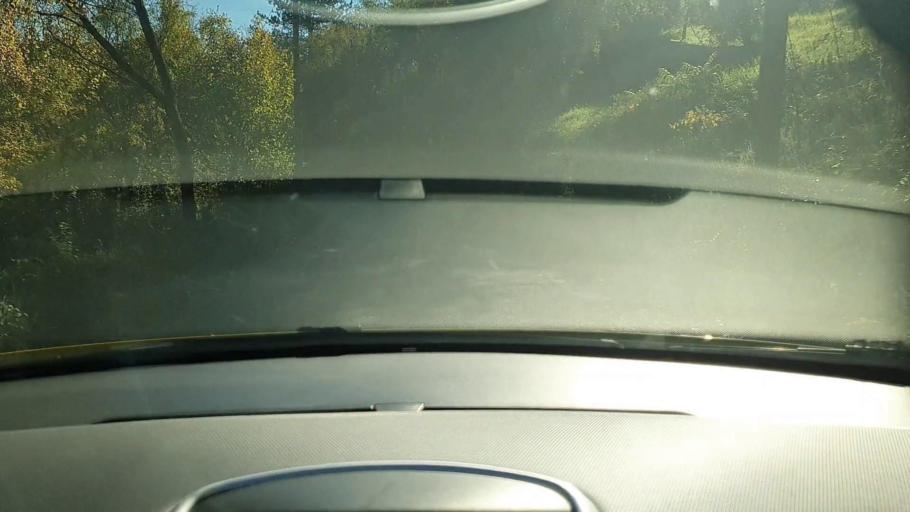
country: FR
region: Languedoc-Roussillon
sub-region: Departement du Gard
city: Le Vigan
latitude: 43.9954
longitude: 3.6203
